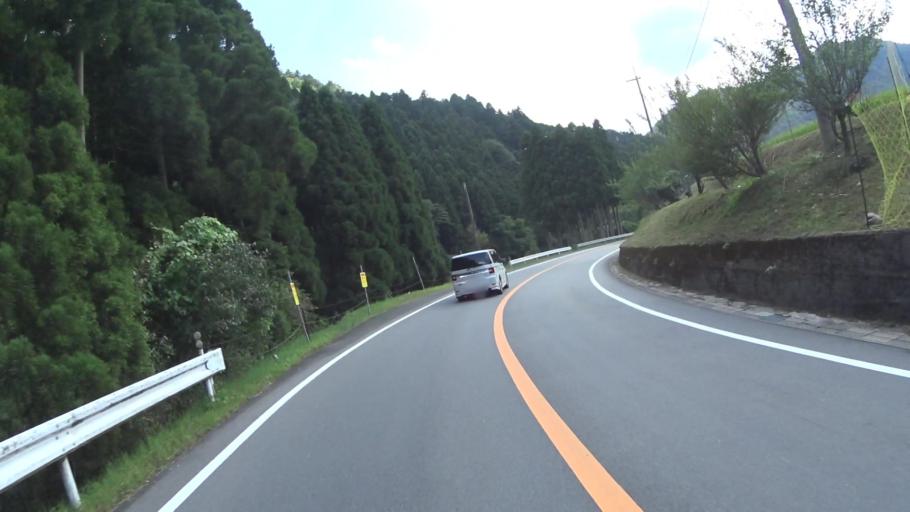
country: JP
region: Kyoto
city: Maizuru
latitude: 35.2917
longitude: 135.5575
